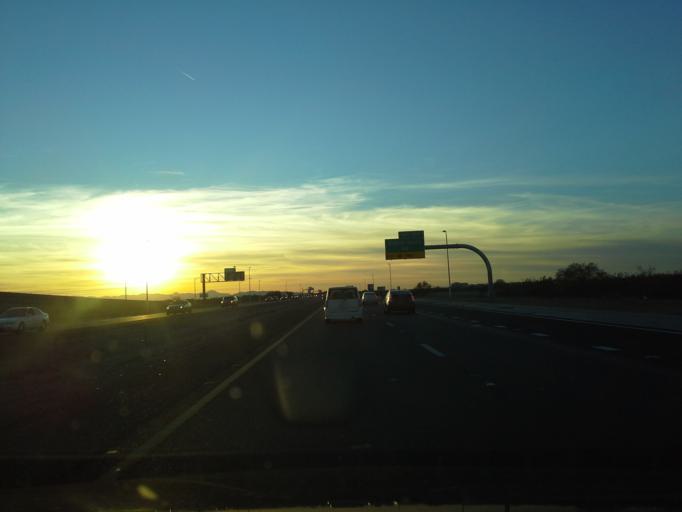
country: US
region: Arizona
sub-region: Pinal County
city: Apache Junction
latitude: 33.3867
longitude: -111.5815
